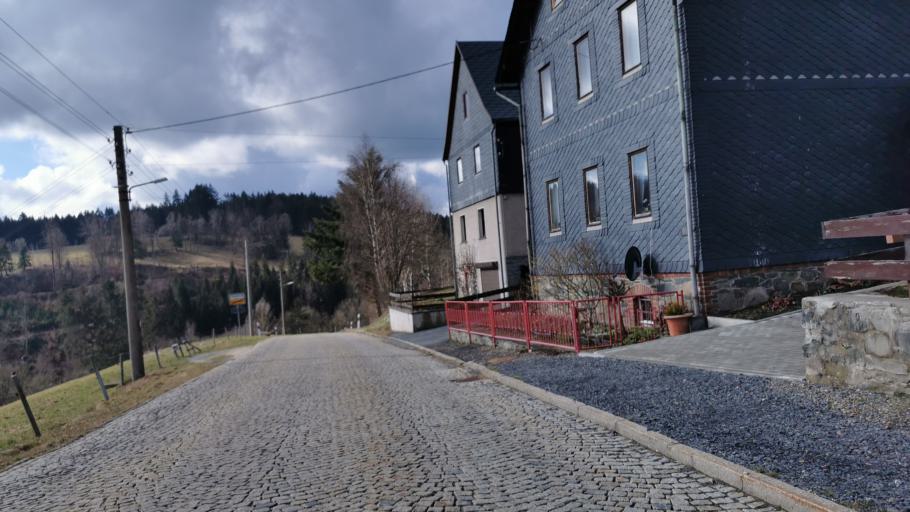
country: DE
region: Thuringia
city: Wurzbach
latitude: 50.4908
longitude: 11.4807
